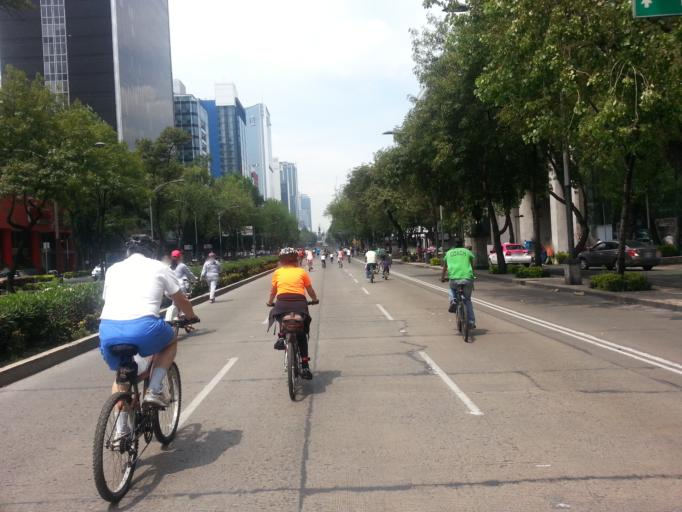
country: MX
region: Mexico City
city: Cuauhtemoc
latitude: 19.4328
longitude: -99.1555
